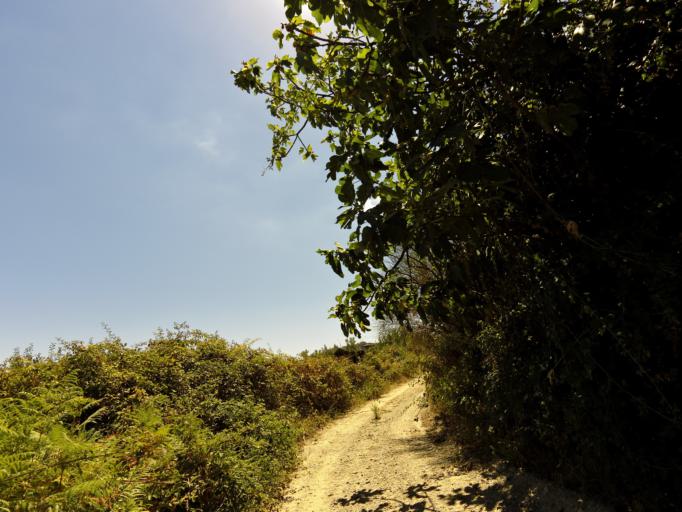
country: IT
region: Calabria
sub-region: Provincia di Reggio Calabria
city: Stilo
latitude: 38.4596
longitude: 16.4624
